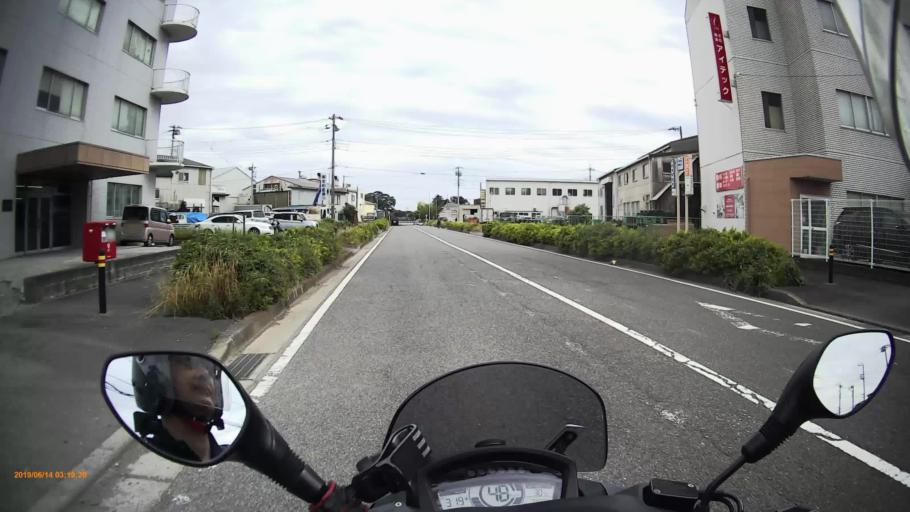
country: JP
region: Kanagawa
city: Minami-rinkan
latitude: 35.4164
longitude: 139.4533
